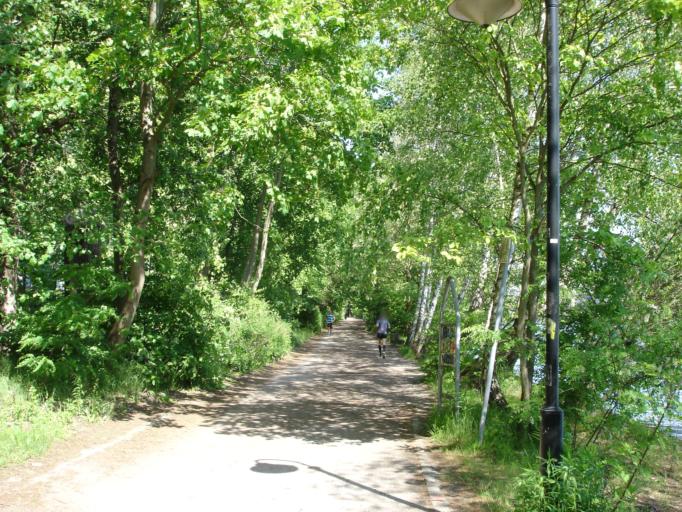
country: DE
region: Berlin
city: Rummelsburg
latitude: 52.4826
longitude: 13.4943
